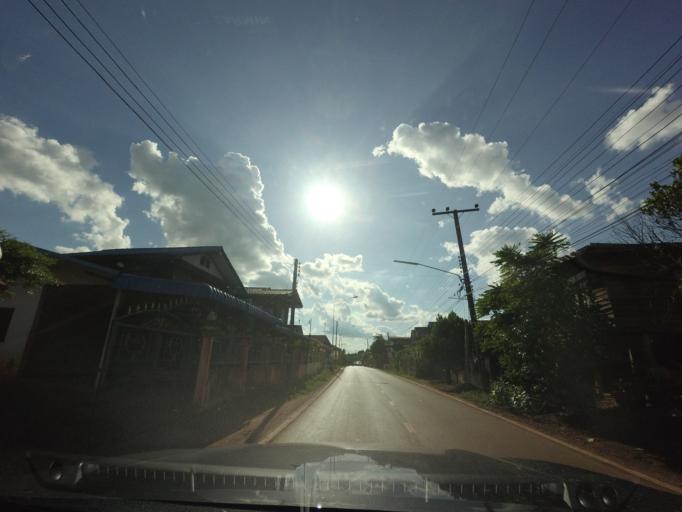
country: TH
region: Changwat Udon Thani
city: Ban Dung
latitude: 17.7464
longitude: 103.3282
